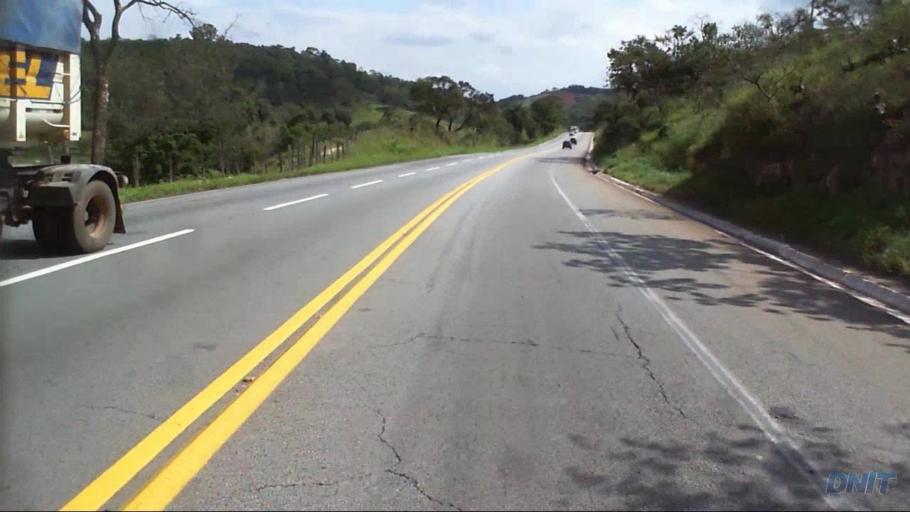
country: BR
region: Minas Gerais
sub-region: Santa Luzia
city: Santa Luzia
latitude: -19.8092
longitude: -43.7867
